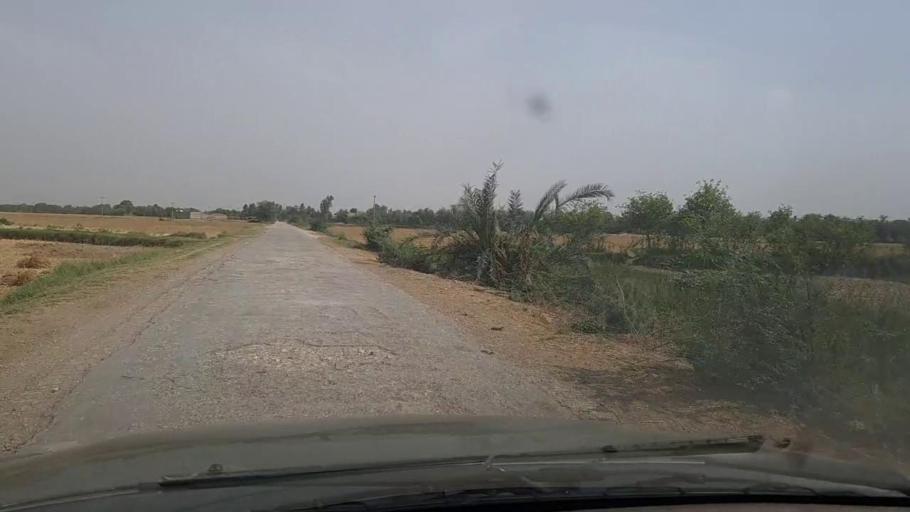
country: PK
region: Sindh
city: Lakhi
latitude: 27.8456
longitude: 68.7573
